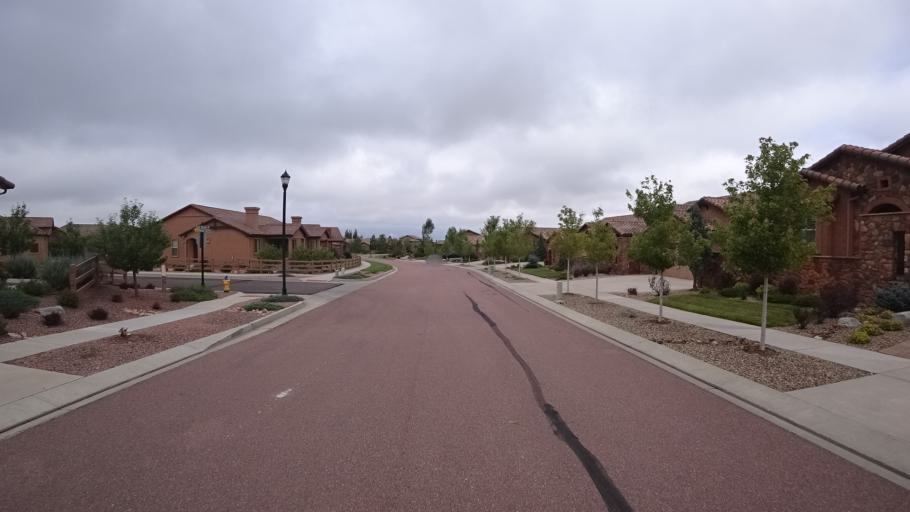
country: US
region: Colorado
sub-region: El Paso County
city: Gleneagle
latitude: 39.0218
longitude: -104.7830
